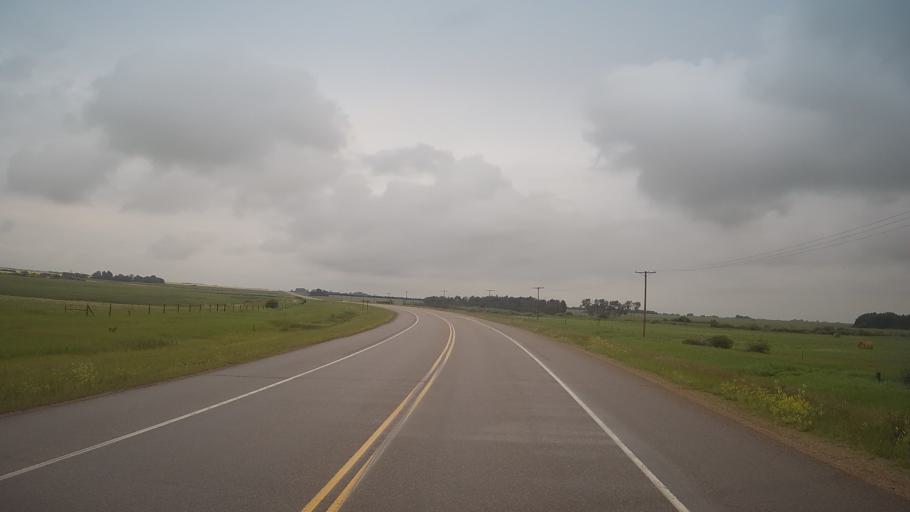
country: CA
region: Saskatchewan
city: Wilkie
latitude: 52.4344
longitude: -108.9306
